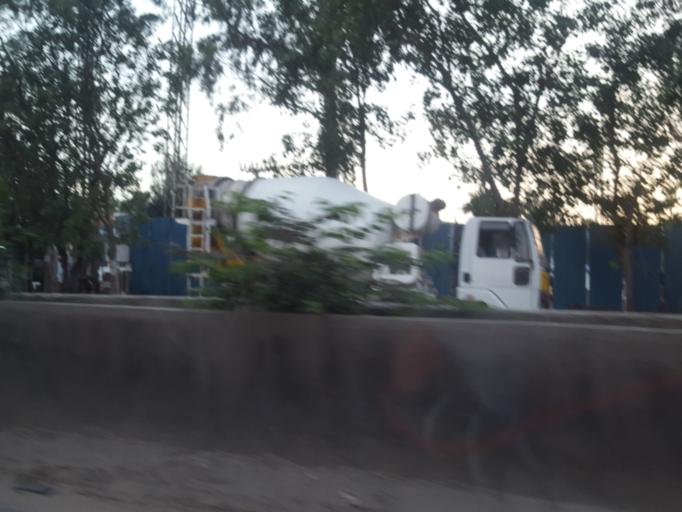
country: IN
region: Telangana
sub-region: Medak
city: Serilingampalle
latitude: 17.5224
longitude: 78.3566
